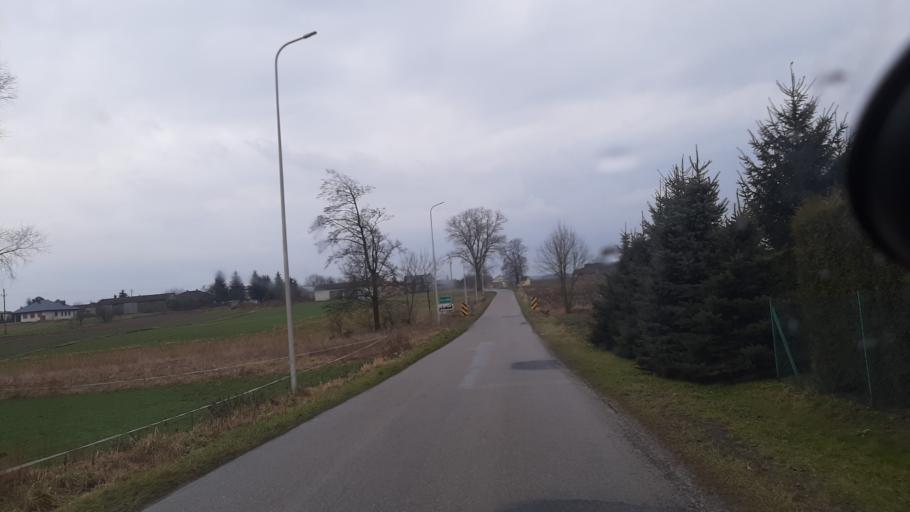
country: PL
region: Lublin Voivodeship
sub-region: Powiat lubelski
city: Jastkow
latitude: 51.3628
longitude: 22.4552
